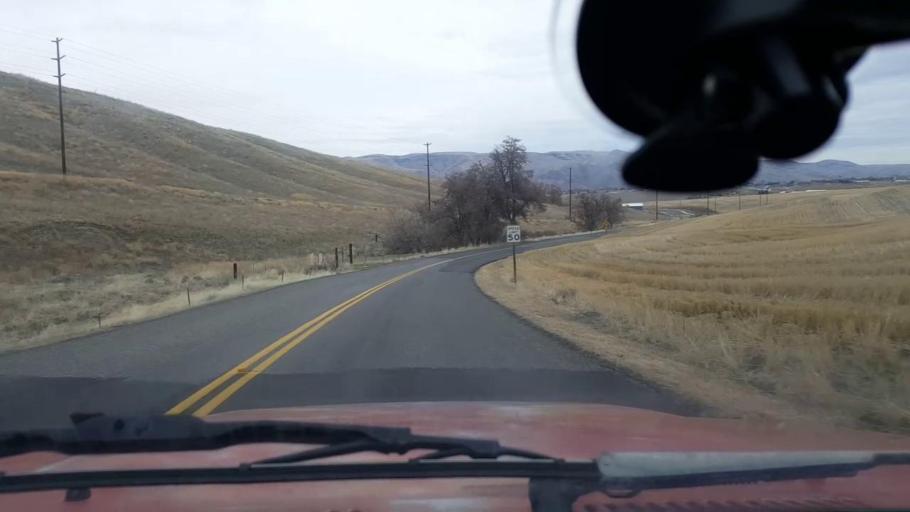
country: US
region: Washington
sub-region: Asotin County
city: Clarkston Heights-Vineland
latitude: 46.3858
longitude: -117.1135
